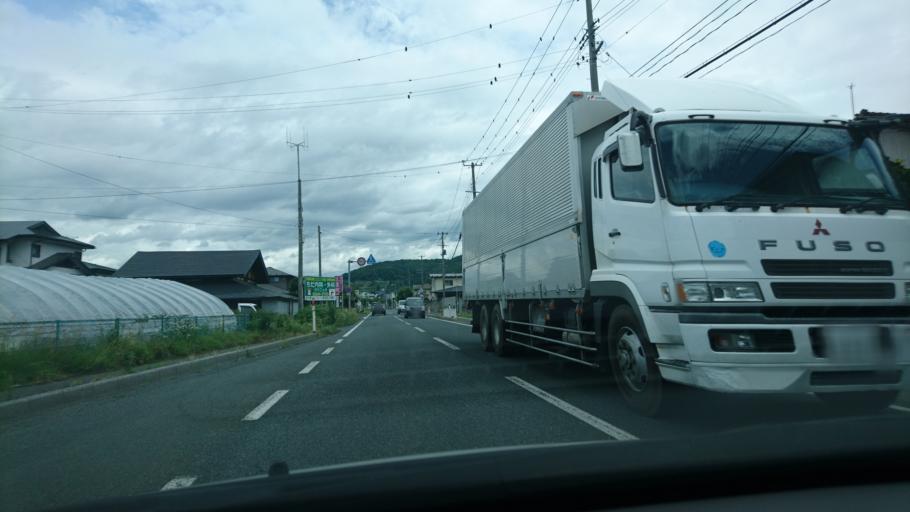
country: JP
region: Iwate
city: Morioka-shi
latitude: 39.6483
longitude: 141.1838
